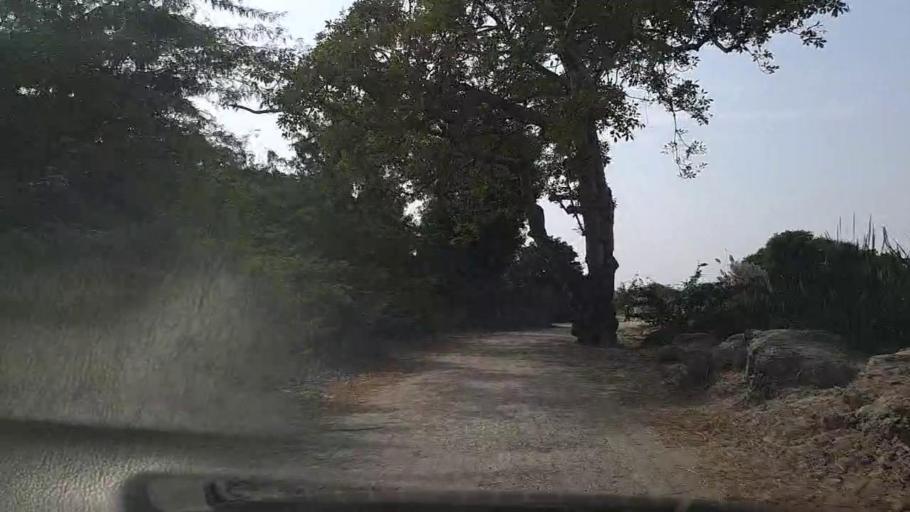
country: PK
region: Sindh
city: Thatta
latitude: 24.7485
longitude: 67.7726
